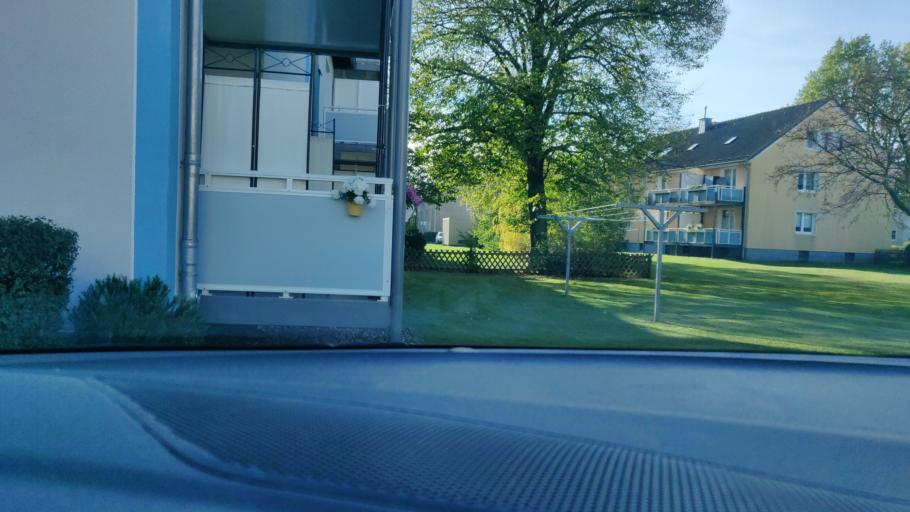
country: DE
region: North Rhine-Westphalia
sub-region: Regierungsbezirk Dusseldorf
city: Velbert
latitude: 51.3506
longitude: 7.0163
